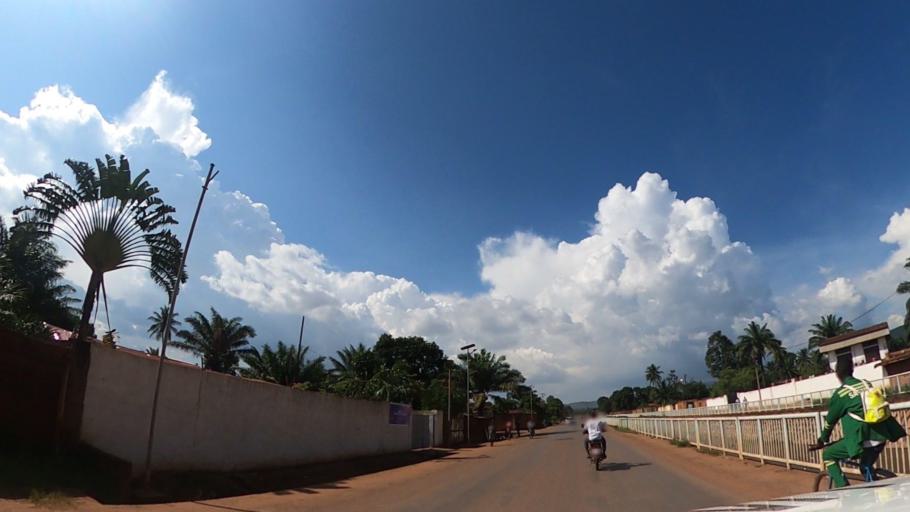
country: CF
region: Bangui
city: Bangui
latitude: 4.3714
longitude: 18.5524
